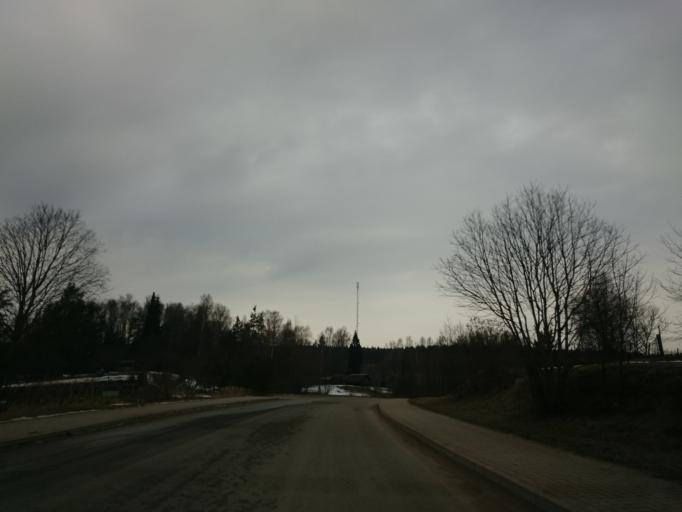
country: LV
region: Cesu Rajons
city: Cesis
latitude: 57.3189
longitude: 25.2573
